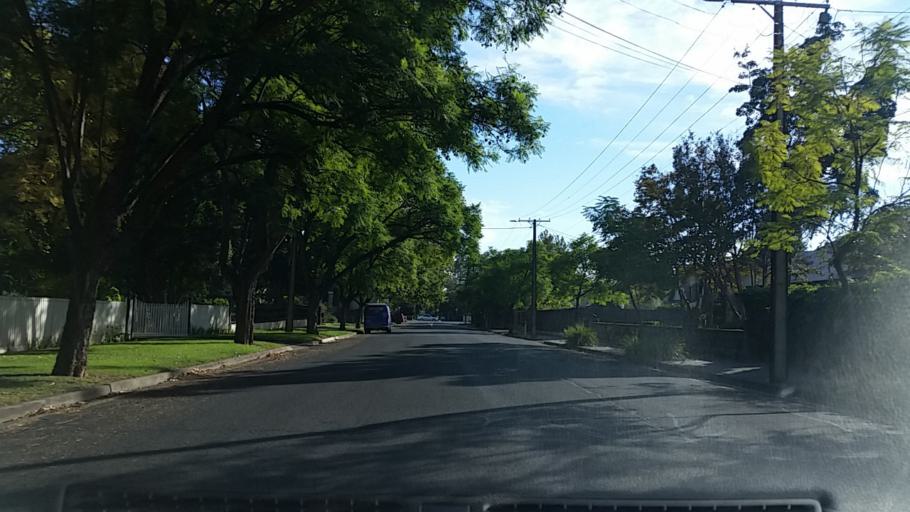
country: AU
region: South Australia
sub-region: Unley
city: Unley Park
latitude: -34.9672
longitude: 138.6026
